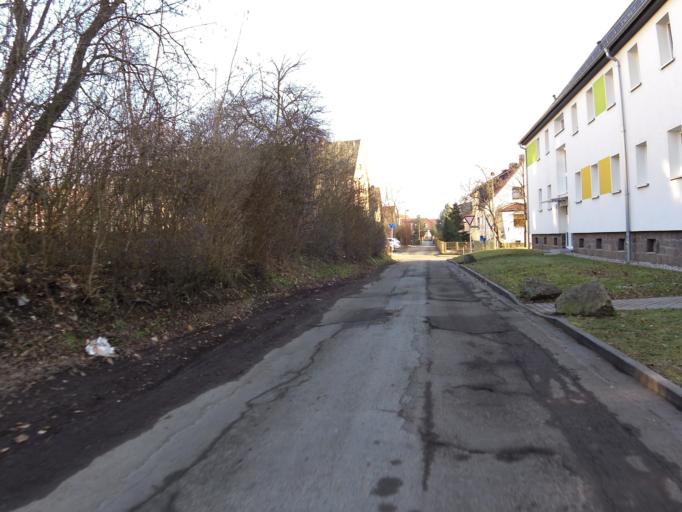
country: DE
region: Saxony
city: Glauchau
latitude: 50.8218
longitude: 12.5560
